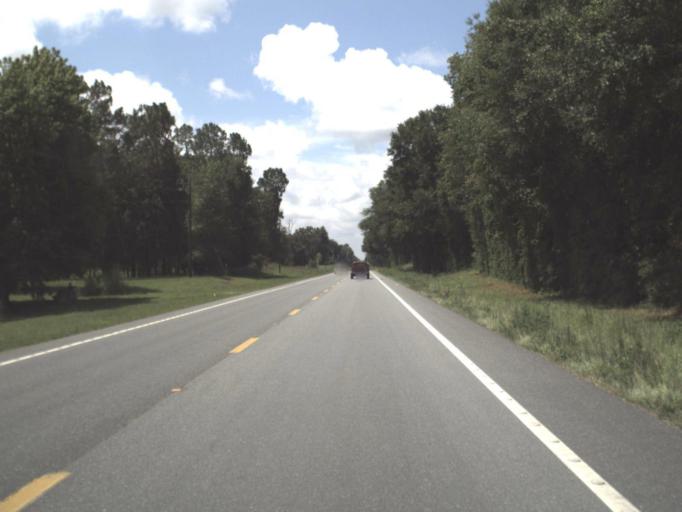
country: US
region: Florida
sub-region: Gilchrist County
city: Trenton
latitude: 29.8198
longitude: -82.8672
